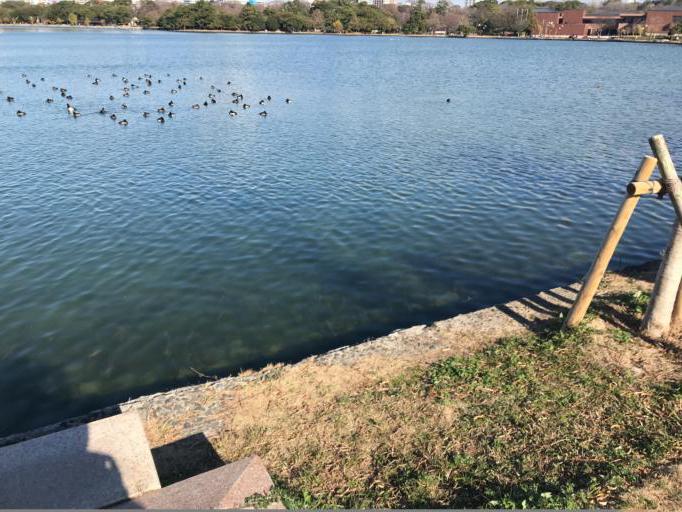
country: JP
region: Fukuoka
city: Fukuoka-shi
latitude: 33.5831
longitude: 130.3758
